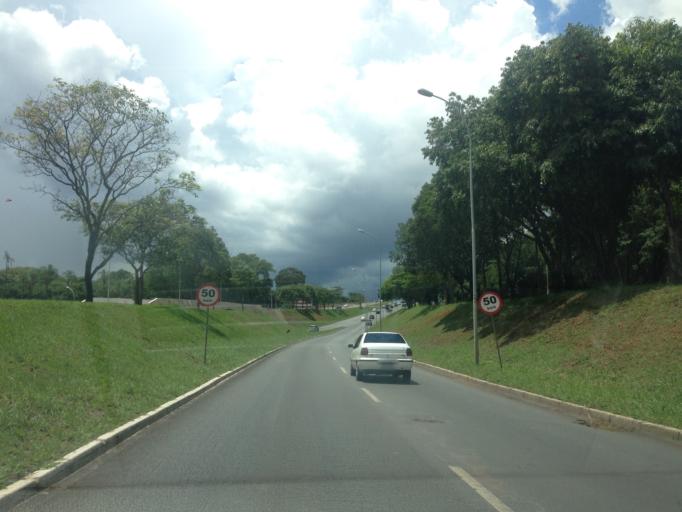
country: BR
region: Federal District
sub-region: Brasilia
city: Brasilia
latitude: -15.8334
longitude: -47.9267
